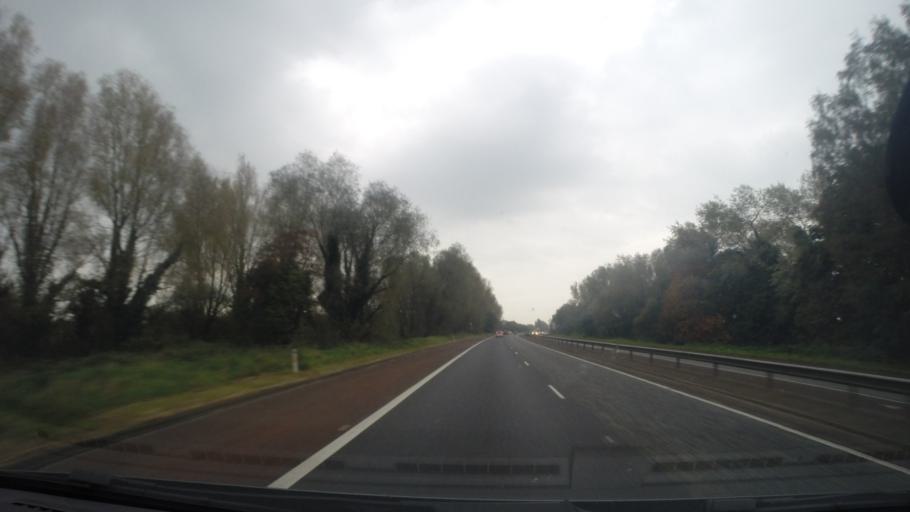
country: GB
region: Northern Ireland
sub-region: Armagh District
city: Portadown
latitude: 54.4824
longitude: -6.5208
